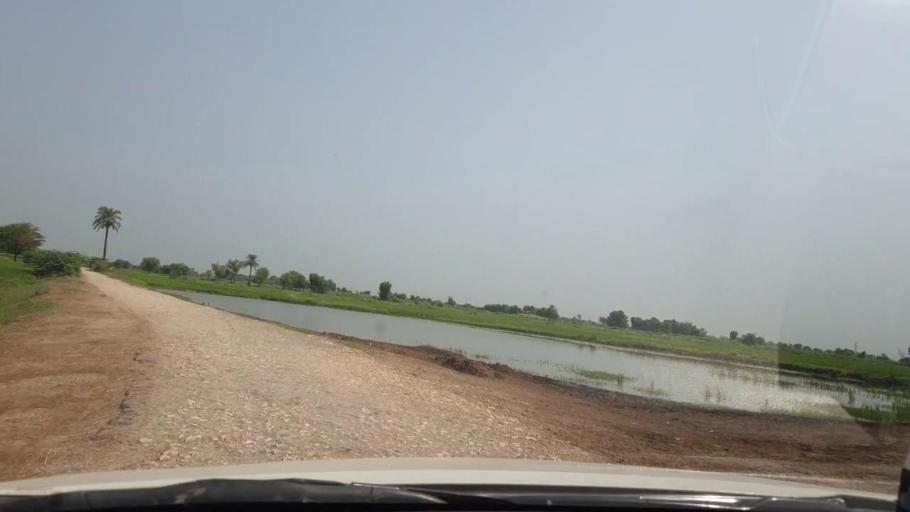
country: PK
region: Sindh
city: Shikarpur
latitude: 27.9593
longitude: 68.7078
